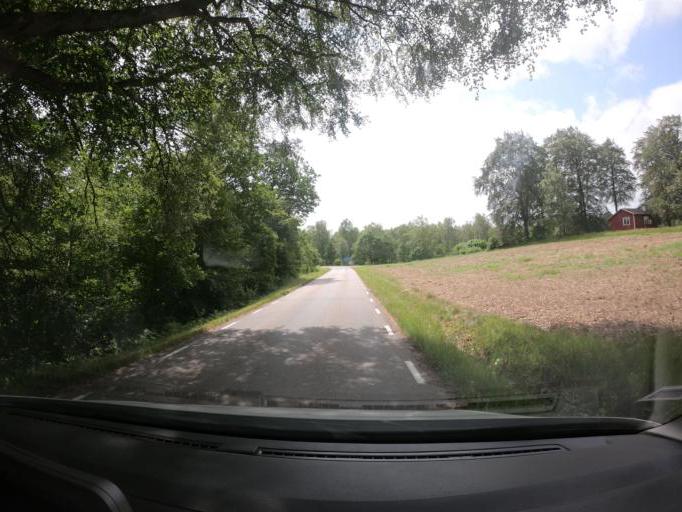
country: SE
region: Skane
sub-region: Hassleholms Kommun
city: Sosdala
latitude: 56.0579
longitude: 13.6022
